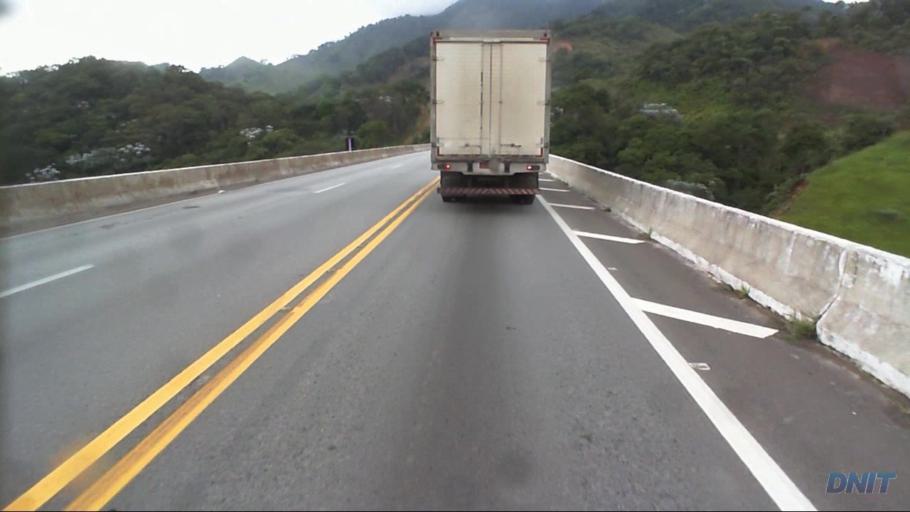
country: BR
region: Minas Gerais
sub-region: Nova Era
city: Nova Era
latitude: -19.6551
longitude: -42.9559
